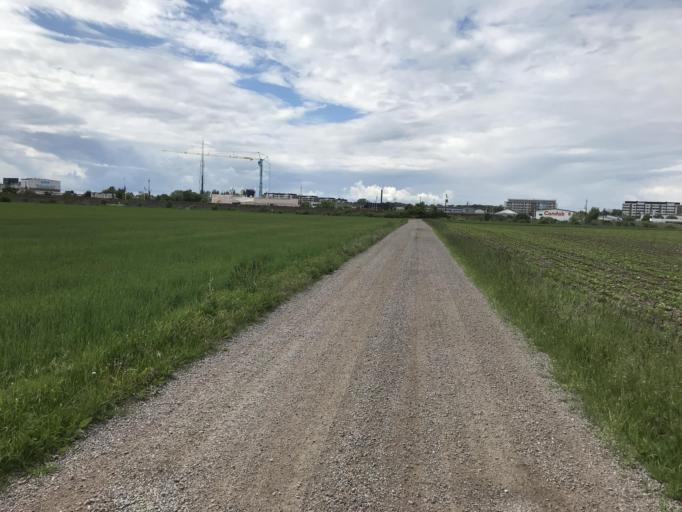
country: SE
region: Skane
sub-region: Landskrona
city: Landskrona
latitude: 55.8875
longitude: 12.8591
